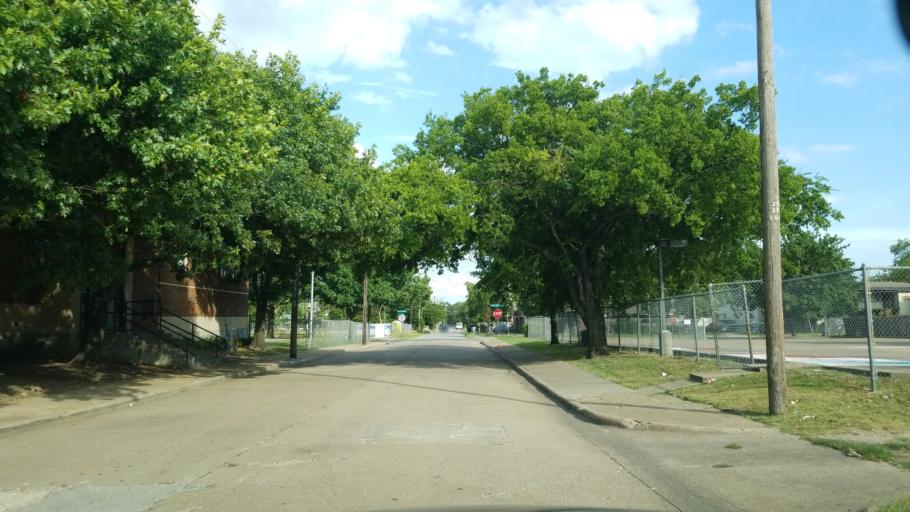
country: US
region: Texas
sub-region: Dallas County
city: Highland Park
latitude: 32.8051
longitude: -96.7766
